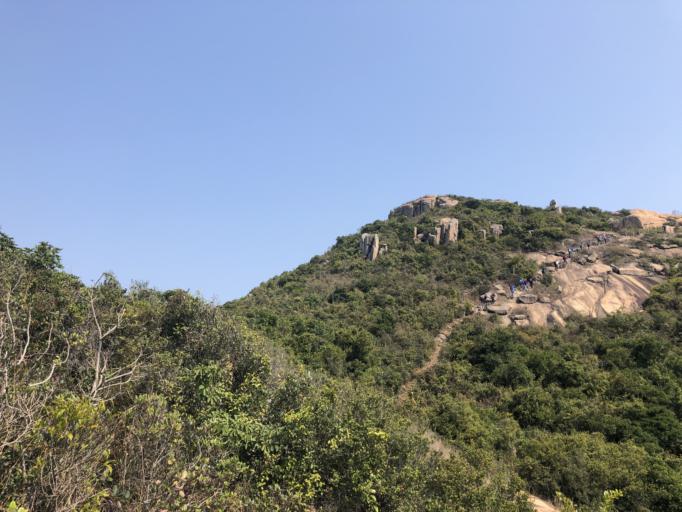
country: HK
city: Sok Kwu Wan
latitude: 22.1670
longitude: 114.2522
